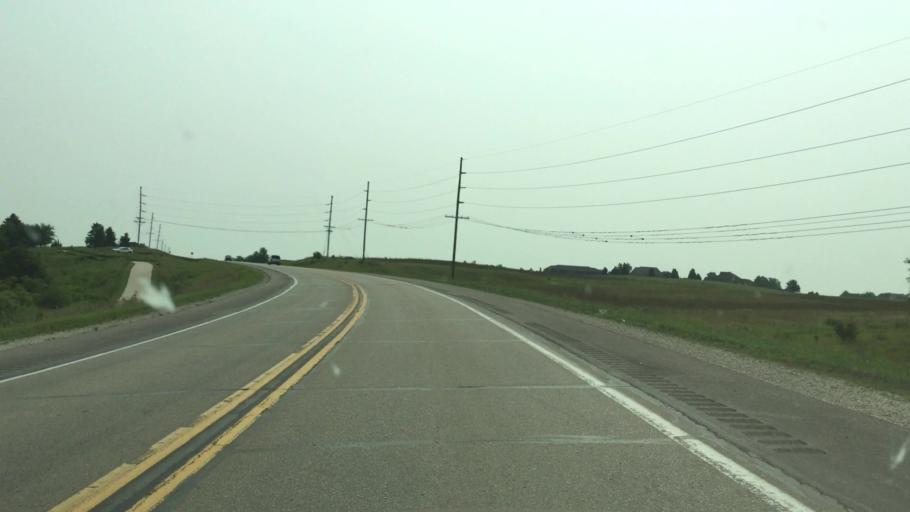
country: US
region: Iowa
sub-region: Dickinson County
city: Milford
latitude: 43.3426
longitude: -95.1751
